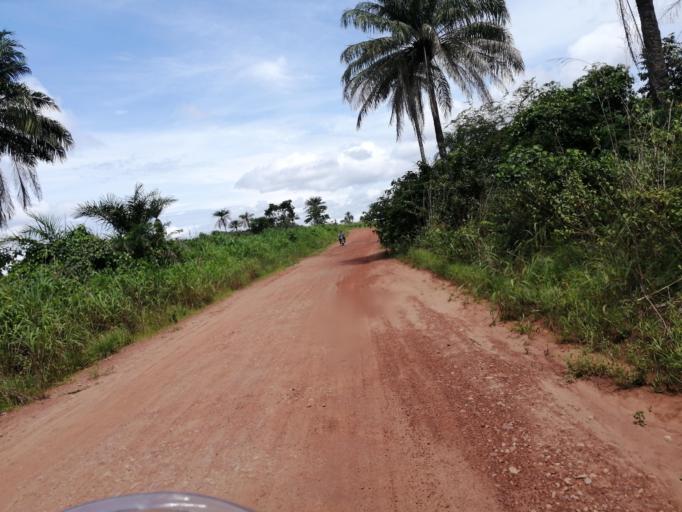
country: SL
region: Northern Province
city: Pepel
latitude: 8.6211
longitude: -13.0388
